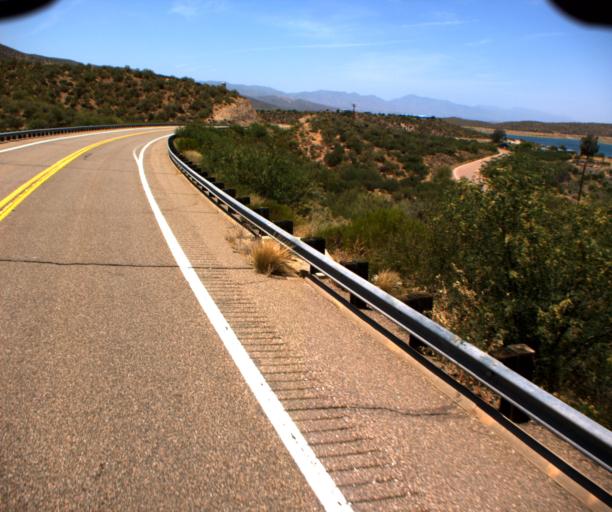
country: US
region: Arizona
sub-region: Gila County
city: Tonto Basin
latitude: 33.6646
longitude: -111.1259
